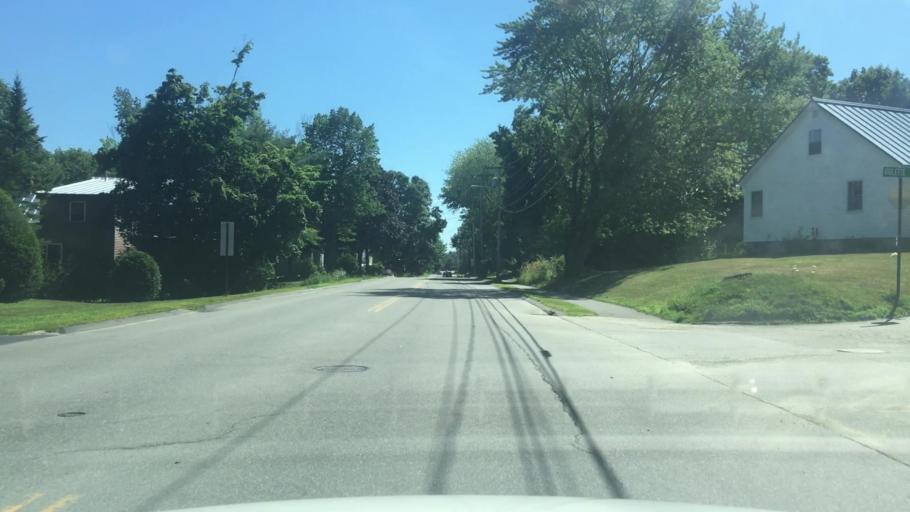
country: US
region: Maine
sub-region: Kennebec County
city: Waterville
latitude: 44.5455
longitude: -69.6458
